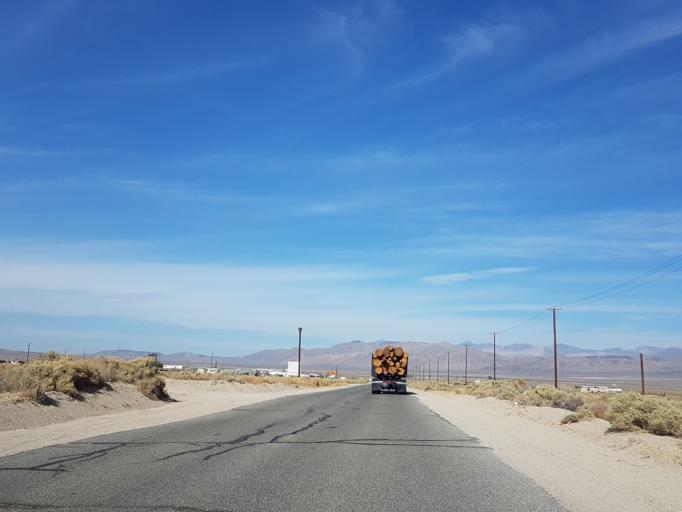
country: US
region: California
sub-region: San Bernardino County
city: Searles Valley
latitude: 35.7969
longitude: -117.3541
